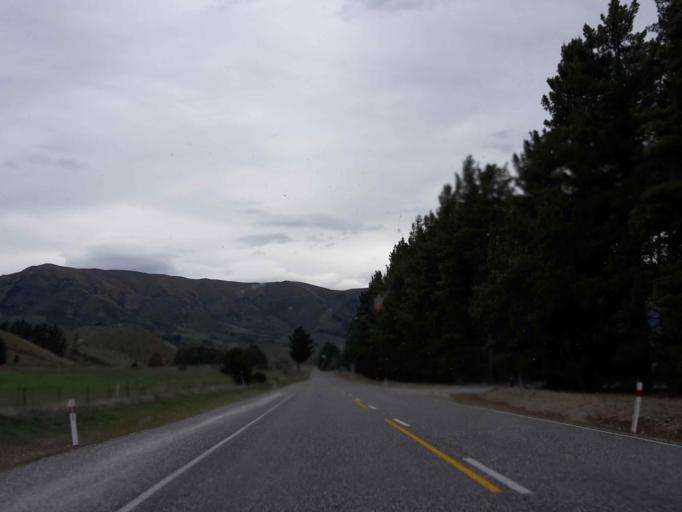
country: NZ
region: Otago
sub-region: Queenstown-Lakes District
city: Wanaka
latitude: -44.7334
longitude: 169.2897
